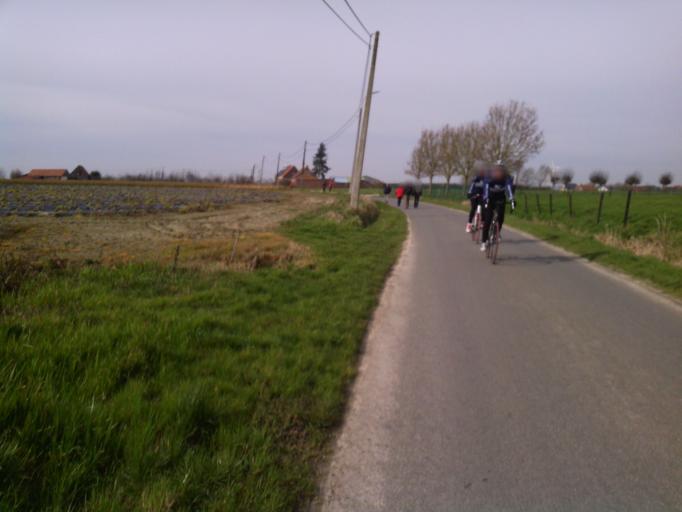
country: BE
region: Flanders
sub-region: Provincie West-Vlaanderen
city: Poperinge
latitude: 50.8501
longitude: 2.8024
